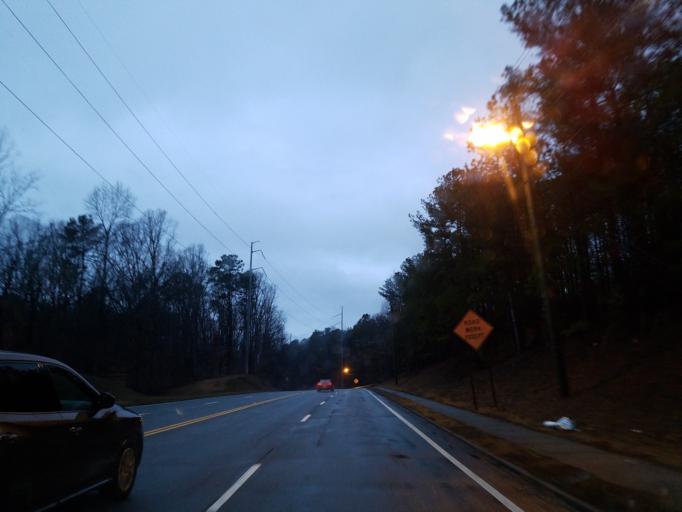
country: US
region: Georgia
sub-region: Fulton County
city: Roswell
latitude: 34.0094
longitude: -84.3007
